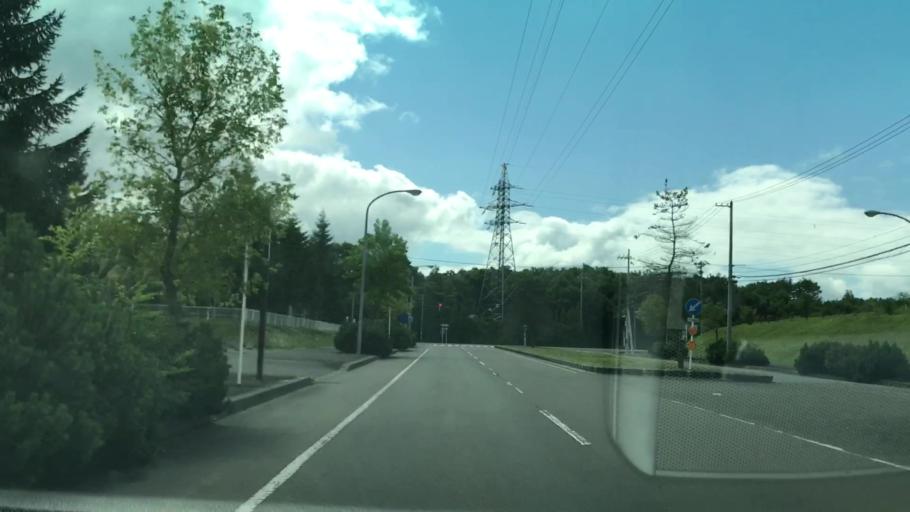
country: JP
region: Hokkaido
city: Chitose
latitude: 42.7736
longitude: 141.6167
